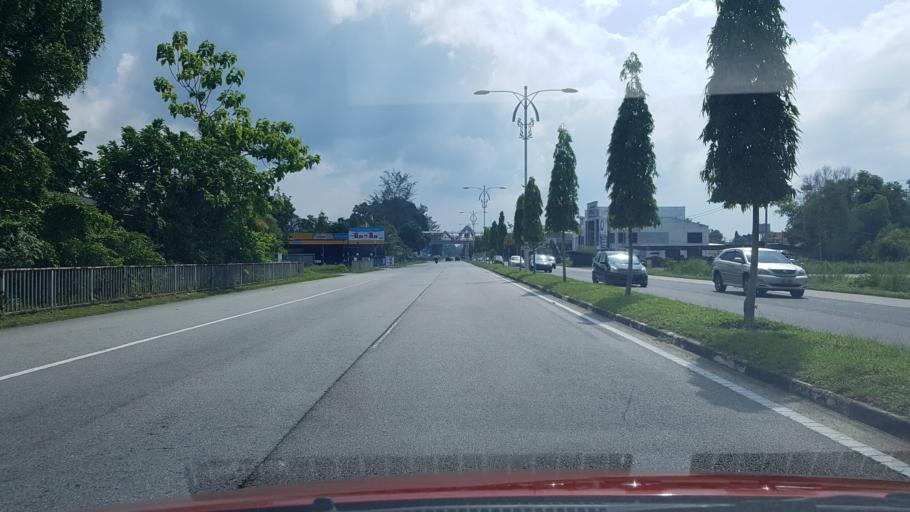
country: MY
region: Terengganu
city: Kuala Terengganu
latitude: 5.3391
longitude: 103.1078
